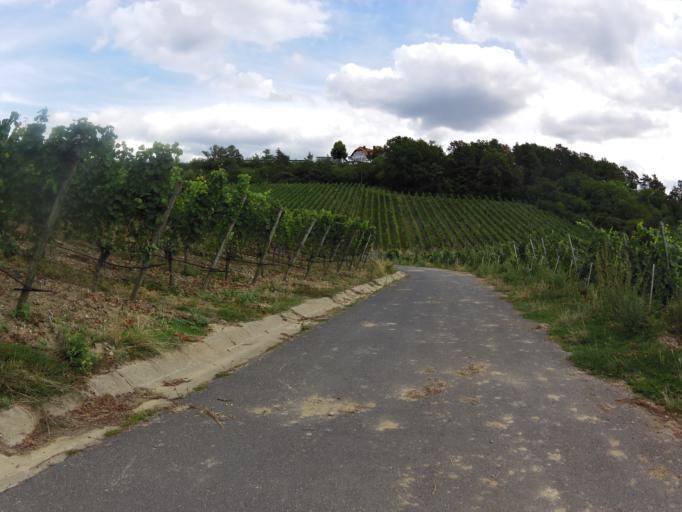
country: DE
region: Bavaria
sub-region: Regierungsbezirk Unterfranken
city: Sommerhausen
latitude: 49.7018
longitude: 10.0319
